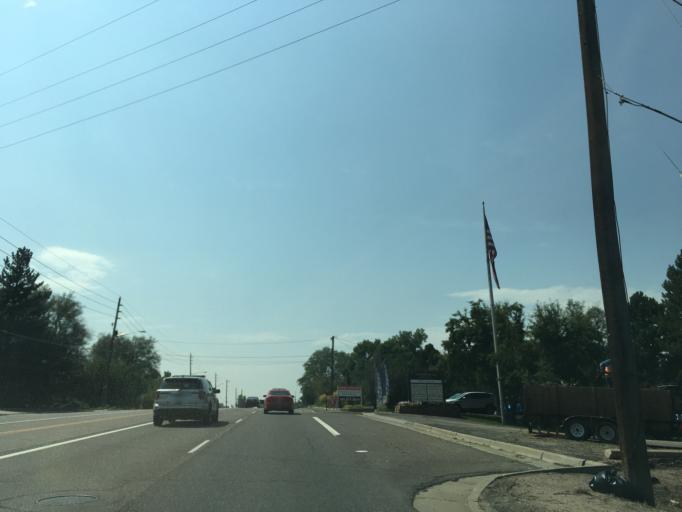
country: US
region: Colorado
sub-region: Jefferson County
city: Wheat Ridge
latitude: 39.7507
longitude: -105.1098
